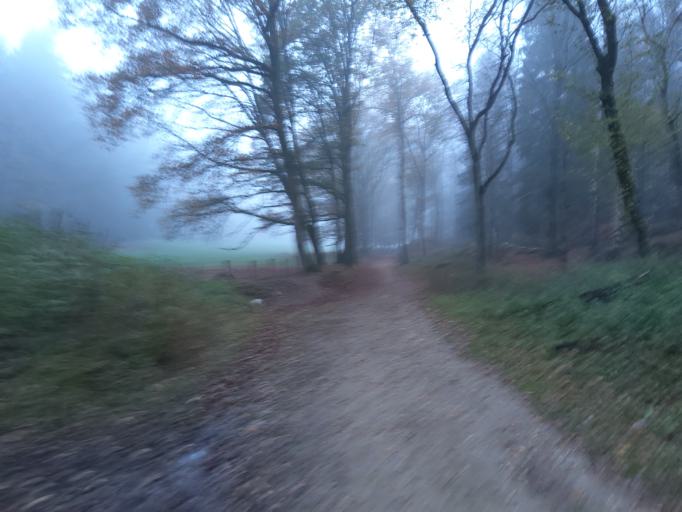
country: NL
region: Gelderland
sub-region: Gemeente Rheden
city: Rheden
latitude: 52.0206
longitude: 6.0227
